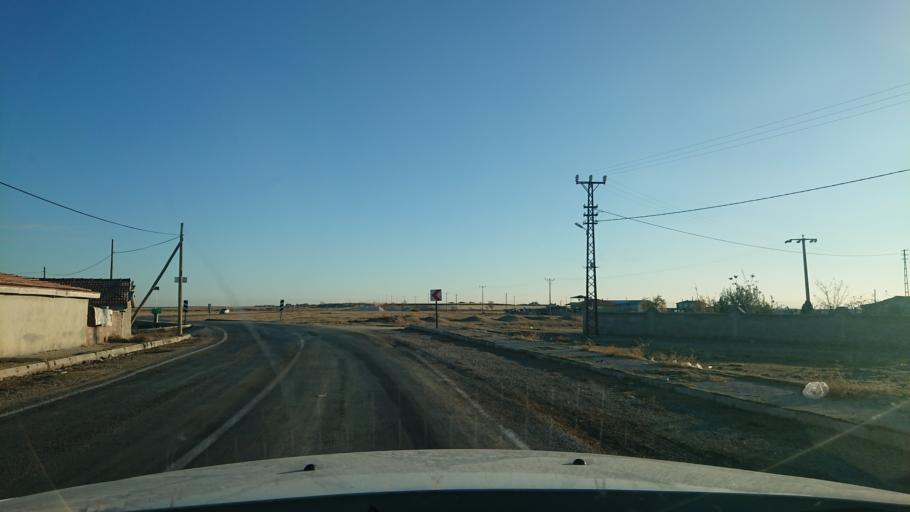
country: TR
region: Aksaray
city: Eskil
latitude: 38.5559
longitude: 33.1998
